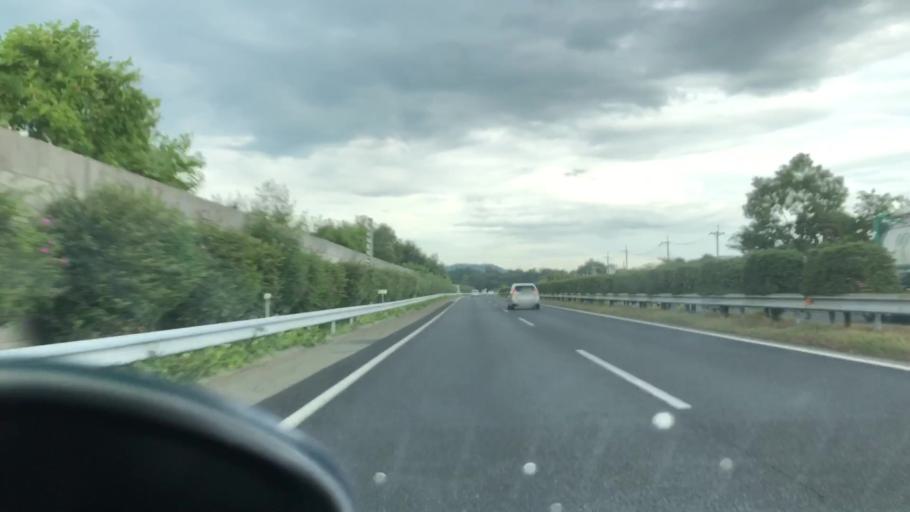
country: JP
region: Hyogo
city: Himeji
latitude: 34.9479
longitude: 134.7894
